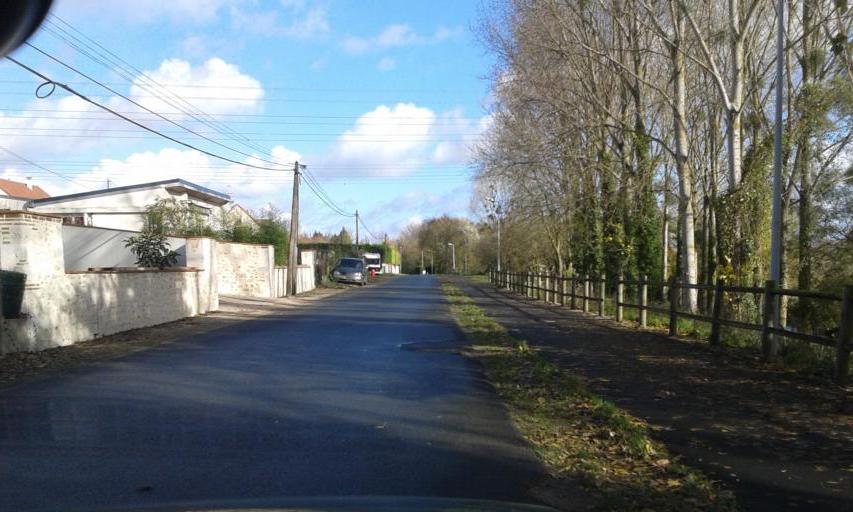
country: FR
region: Centre
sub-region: Departement du Loir-et-Cher
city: Saint-Laurent-Nouan
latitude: 47.7289
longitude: 1.5804
